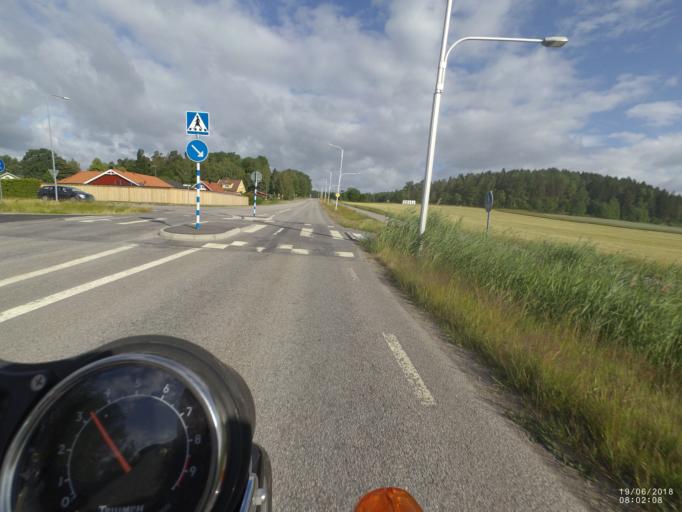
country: SE
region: Soedermanland
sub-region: Nykopings Kommun
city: Nykoping
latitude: 58.7779
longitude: 16.9932
